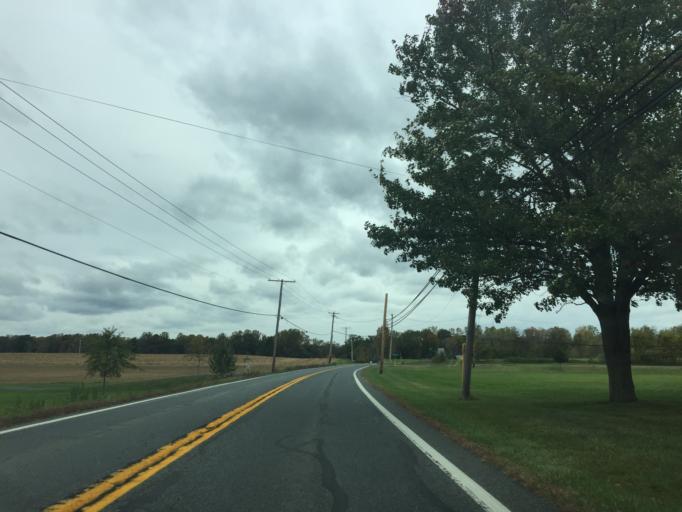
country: US
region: Maryland
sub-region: Harford County
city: Riverside
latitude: 39.5237
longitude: -76.2644
